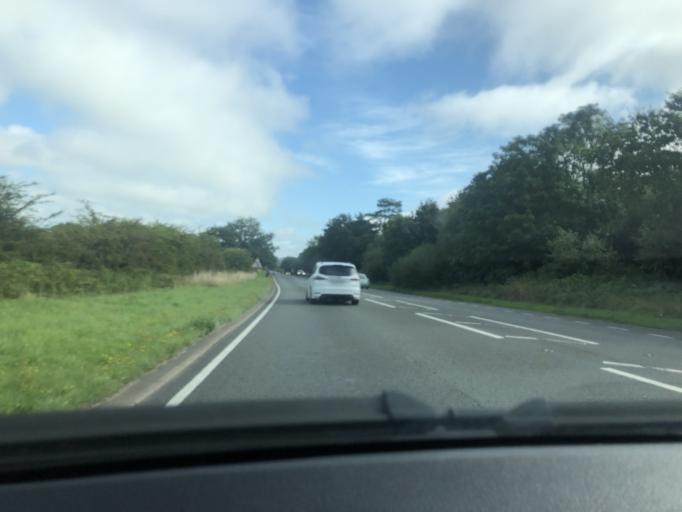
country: GB
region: England
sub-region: Devon
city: Honiton
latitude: 50.8069
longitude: -3.1743
